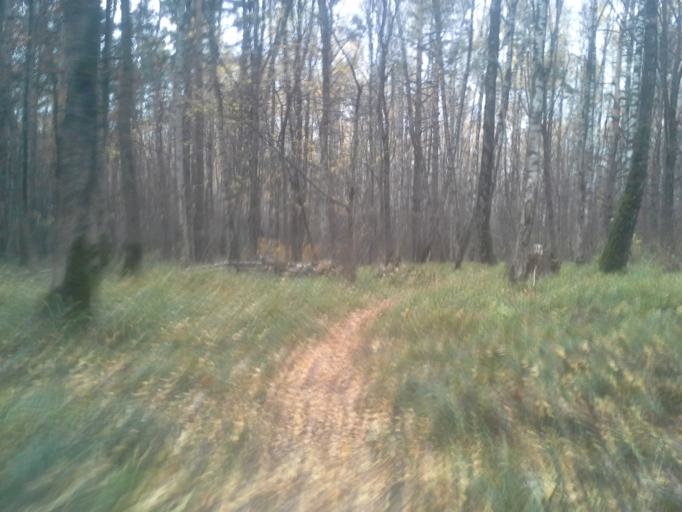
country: RU
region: Moskovskaya
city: Vostryakovo
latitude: 55.6516
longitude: 37.4484
